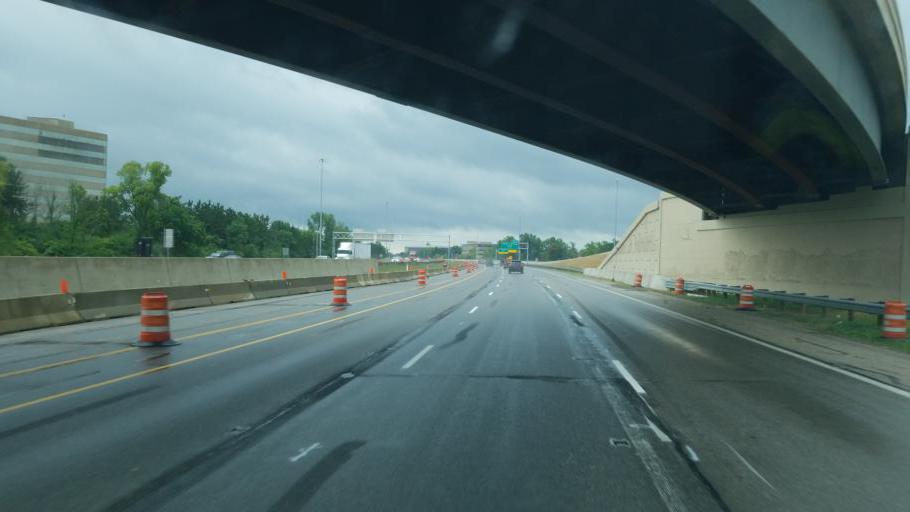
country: US
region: Ohio
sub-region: Franklin County
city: Dublin
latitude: 40.0971
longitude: -83.1360
